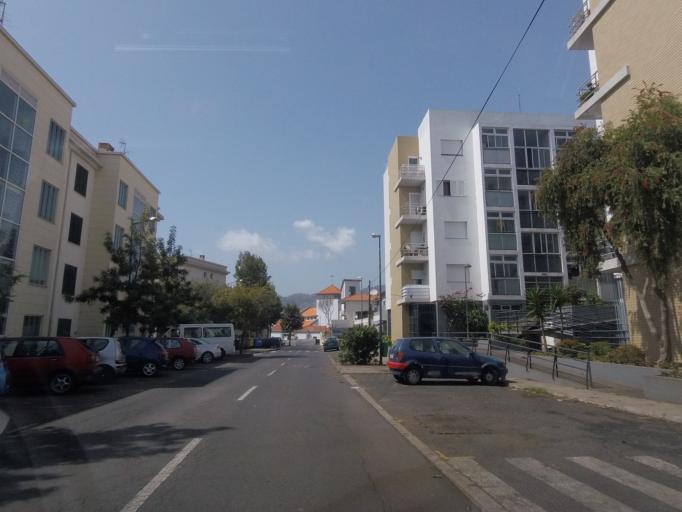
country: PT
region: Madeira
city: Camara de Lobos
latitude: 32.6593
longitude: -16.9466
